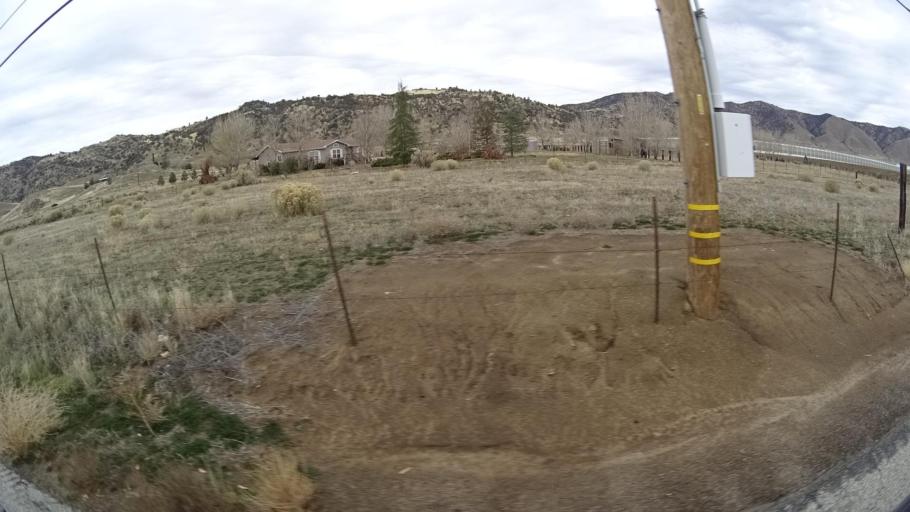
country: US
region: California
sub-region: Kern County
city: Bear Valley Springs
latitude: 35.1235
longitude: -118.6029
